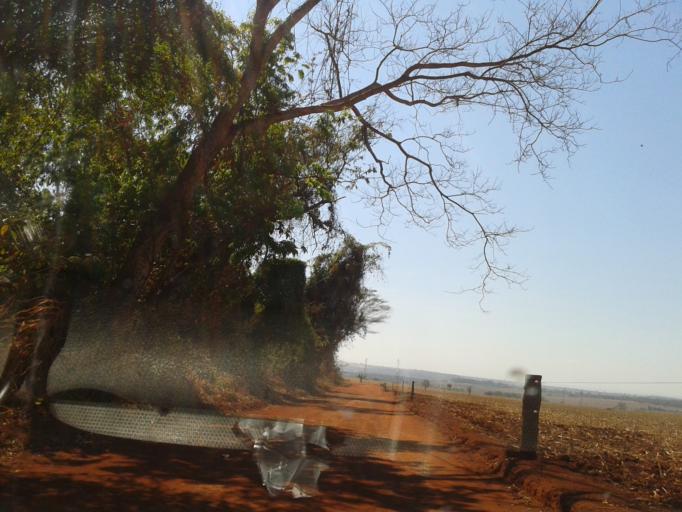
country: BR
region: Minas Gerais
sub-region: Capinopolis
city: Capinopolis
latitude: -18.6179
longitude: -49.4720
